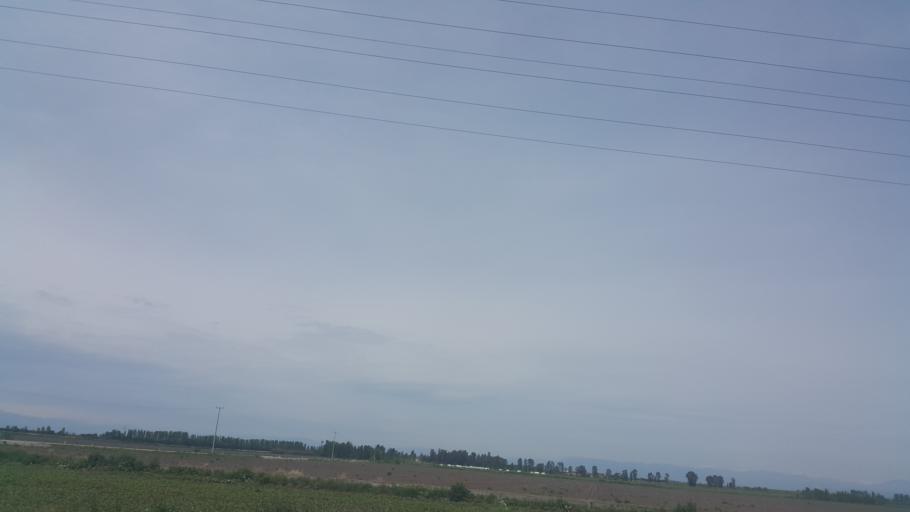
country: TR
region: Adana
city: Kosreli
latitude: 37.0690
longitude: 36.0017
